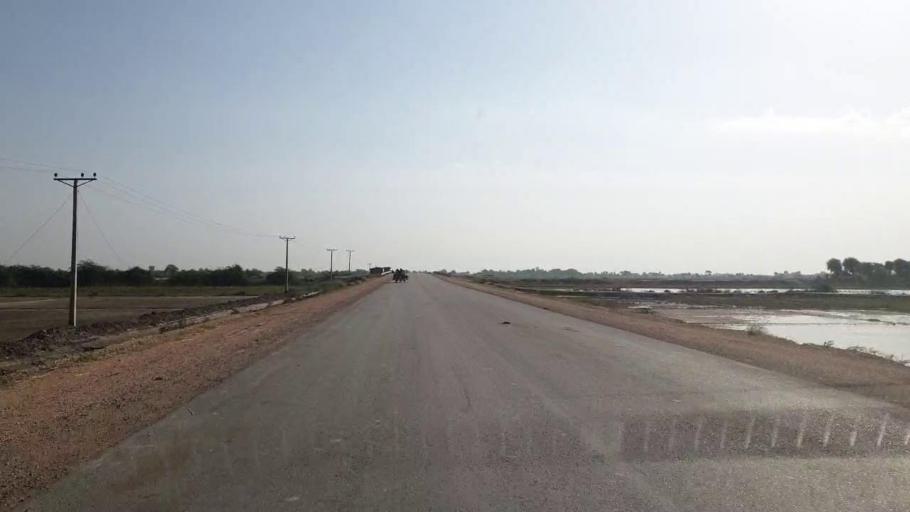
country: PK
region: Sindh
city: Tando Bago
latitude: 24.6568
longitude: 69.0175
